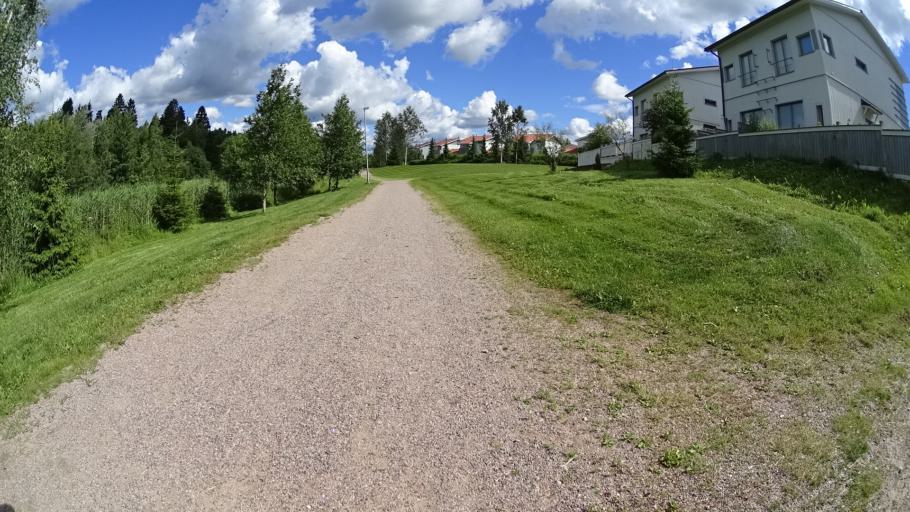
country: FI
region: Uusimaa
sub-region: Helsinki
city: Kirkkonummi
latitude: 60.1566
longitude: 24.5469
